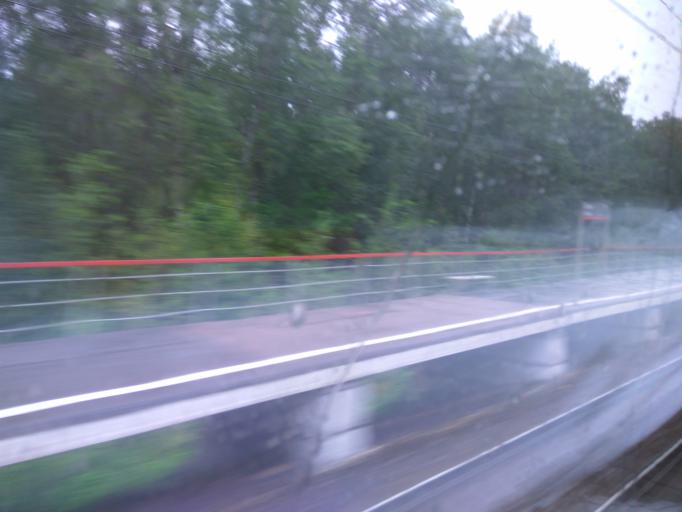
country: RU
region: Moskovskaya
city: Zhilevo
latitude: 55.0273
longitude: 38.0095
